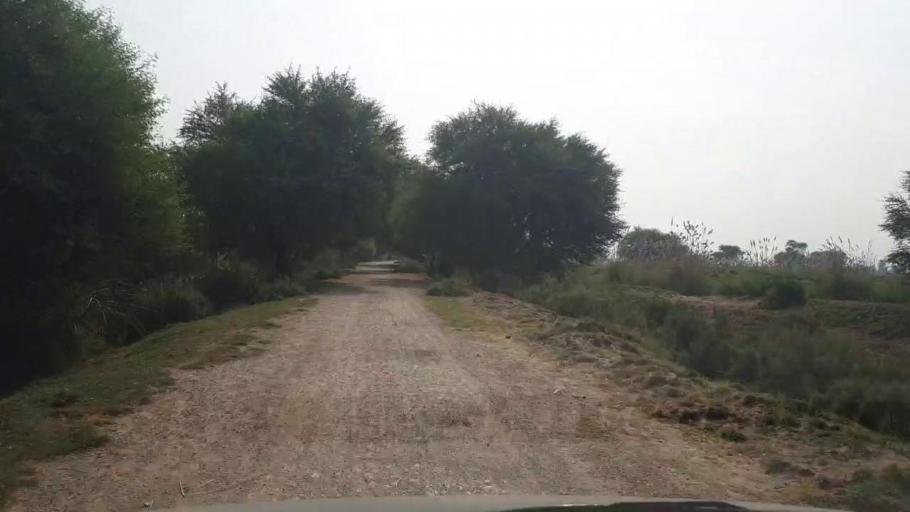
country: PK
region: Sindh
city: Tando Muhammad Khan
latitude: 25.1236
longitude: 68.4373
